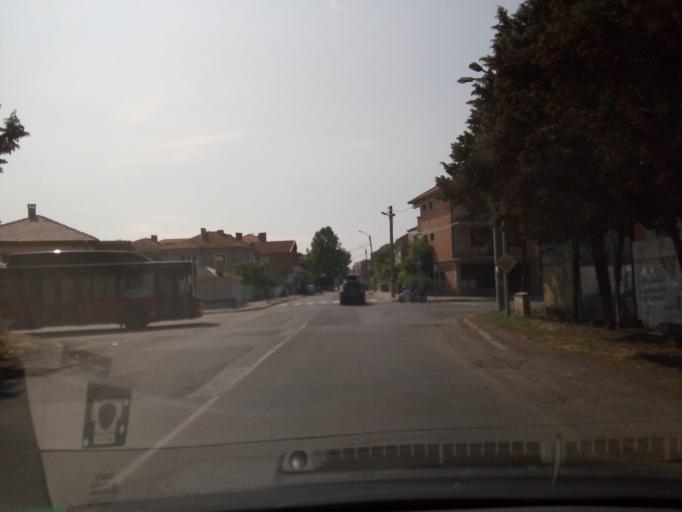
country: BG
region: Burgas
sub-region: Obshtina Pomorie
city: Pomorie
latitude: 42.5715
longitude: 27.6123
